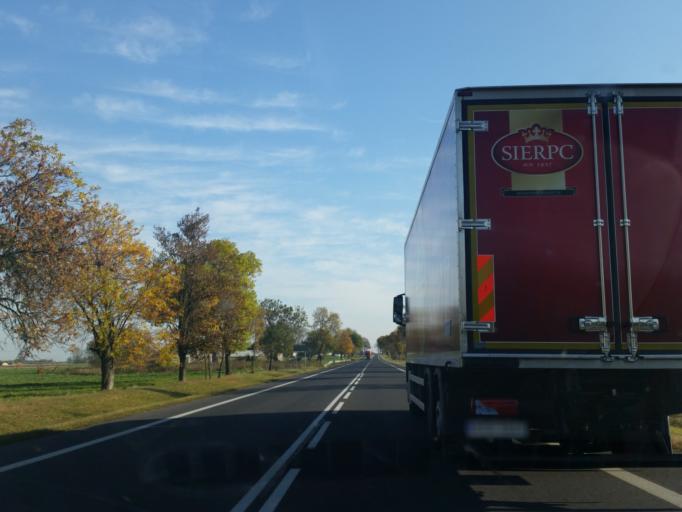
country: PL
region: Masovian Voivodeship
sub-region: Powiat sierpecki
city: Rosciszewo
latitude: 52.8223
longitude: 19.7753
